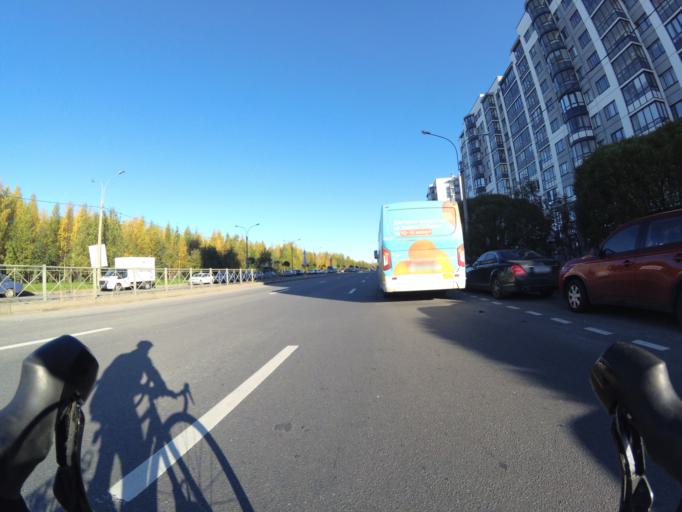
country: RU
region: Leningrad
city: Untolovo
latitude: 60.0044
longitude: 30.1965
